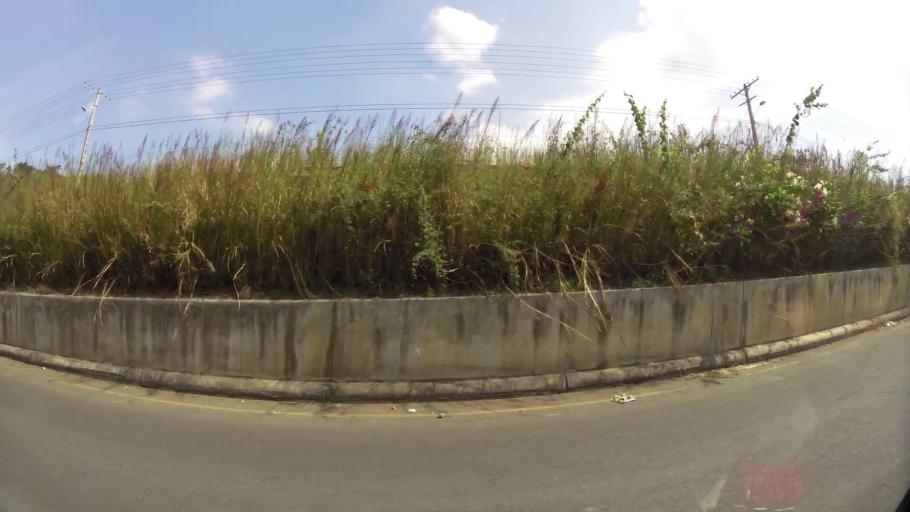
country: EC
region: Guayas
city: El Triunfo
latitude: -2.0321
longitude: -79.9017
